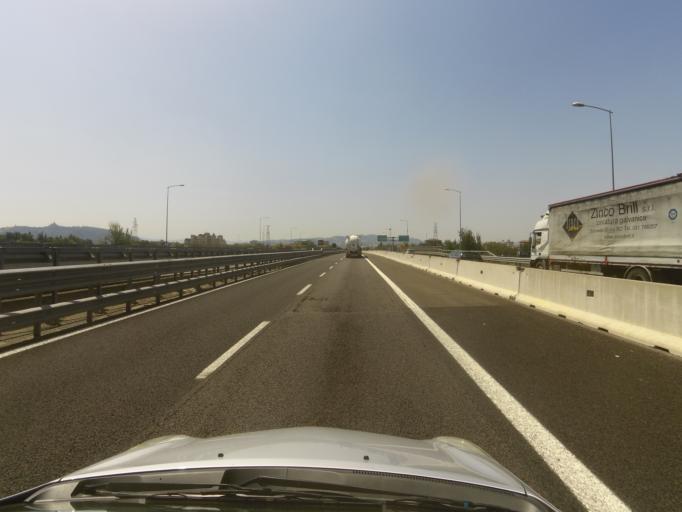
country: IT
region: Emilia-Romagna
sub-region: Provincia di Bologna
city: Calderara di Reno
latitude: 44.5211
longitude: 11.2849
